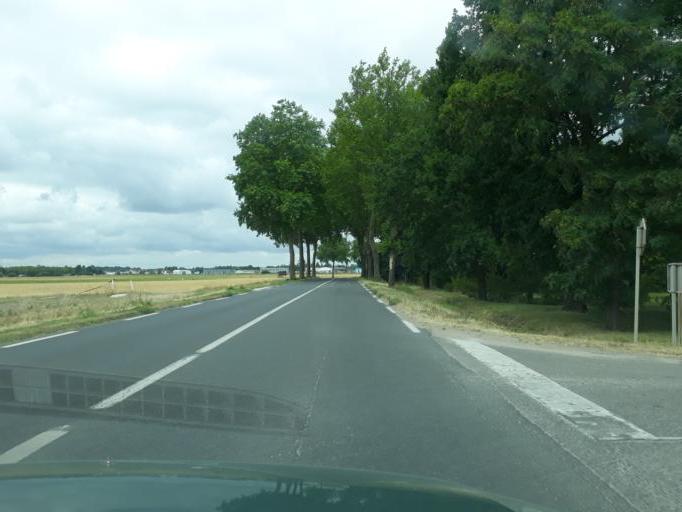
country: FR
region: Centre
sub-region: Departement du Loiret
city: Saint-Denis-en-Val
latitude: 47.8690
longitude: 1.9558
